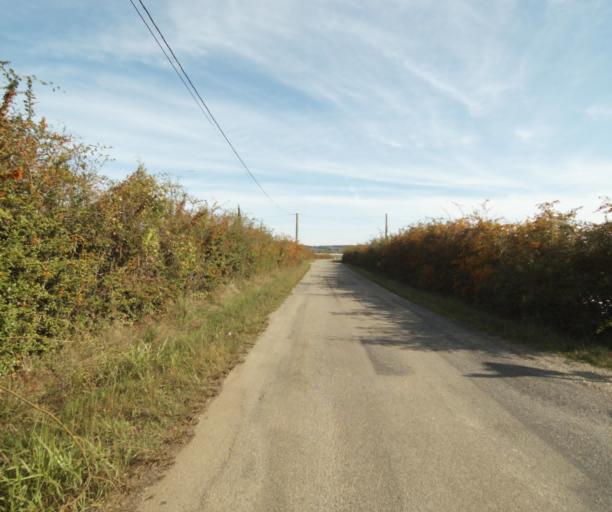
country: FR
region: Midi-Pyrenees
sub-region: Departement du Tarn-et-Garonne
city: Orgueil
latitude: 43.9056
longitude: 1.4196
